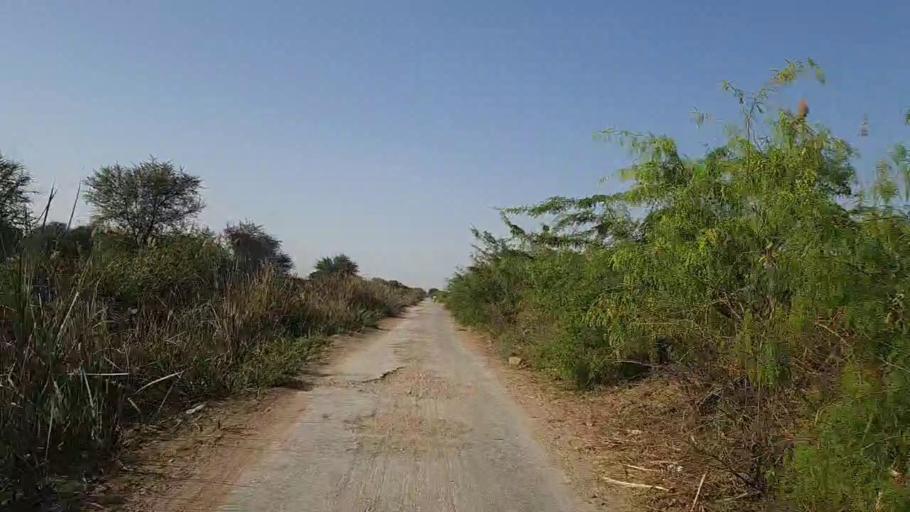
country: PK
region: Sindh
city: Kotri
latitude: 25.1588
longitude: 68.2639
